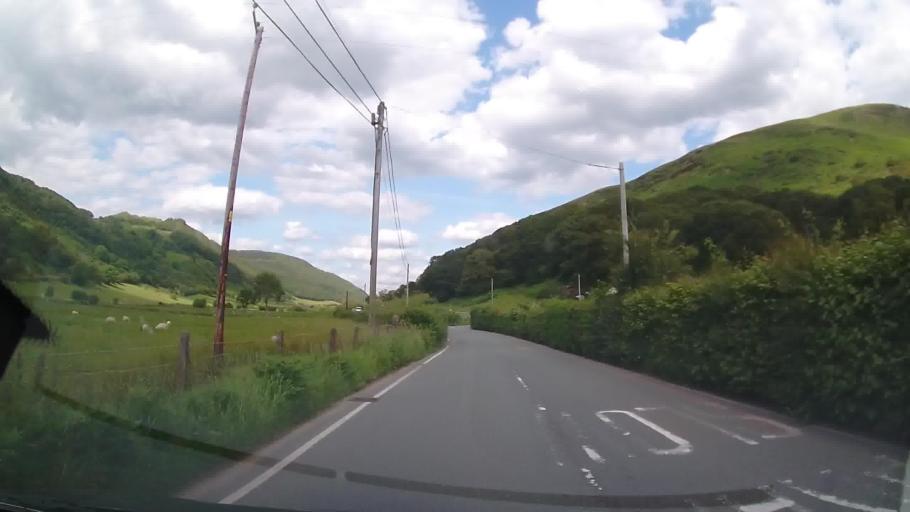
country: GB
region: Wales
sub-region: Gwynedd
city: Tywyn
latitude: 52.6234
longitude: -3.9958
